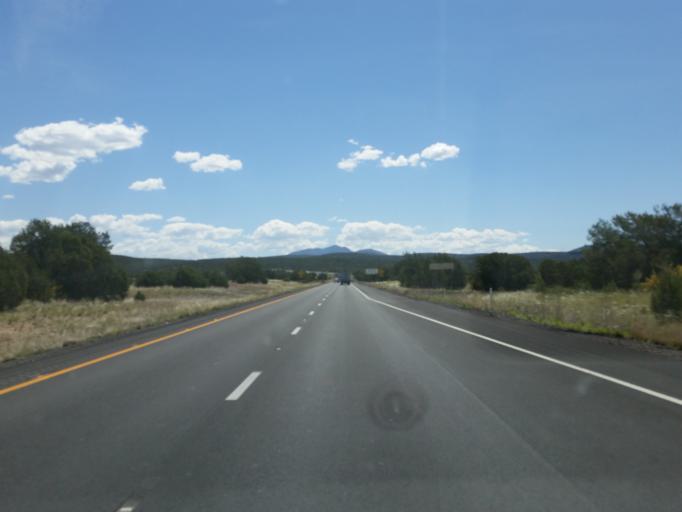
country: US
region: Arizona
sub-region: Coconino County
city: Williams
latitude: 35.2139
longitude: -112.4224
